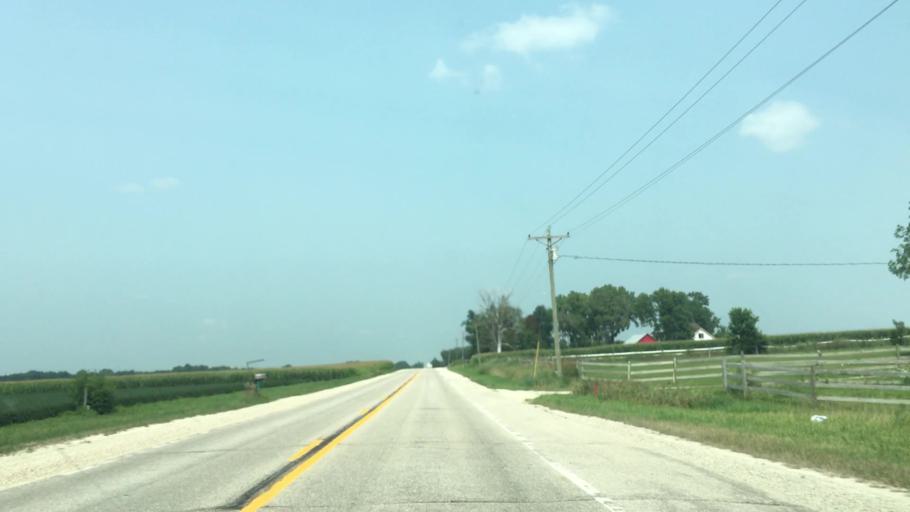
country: US
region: Iowa
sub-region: Benton County
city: Urbana
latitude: 42.3440
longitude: -91.8893
